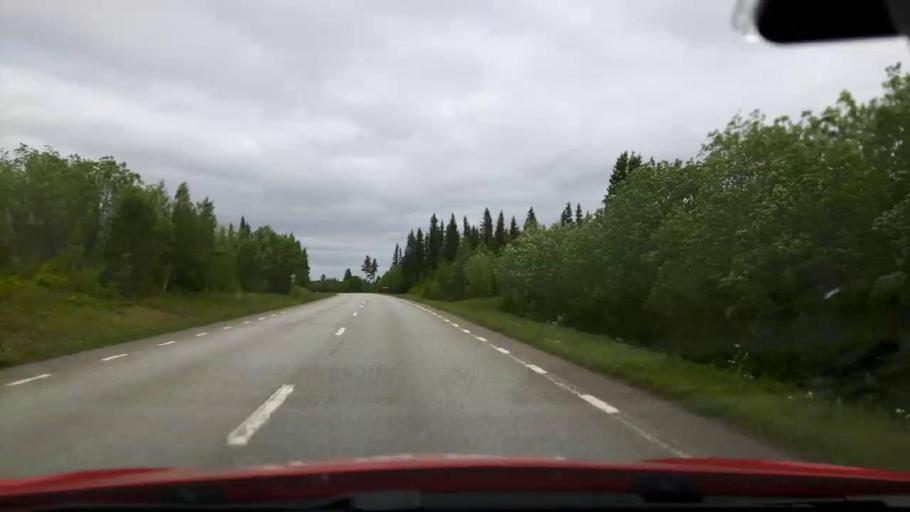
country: SE
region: Jaemtland
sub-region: Krokoms Kommun
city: Krokom
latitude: 63.5721
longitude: 14.6272
